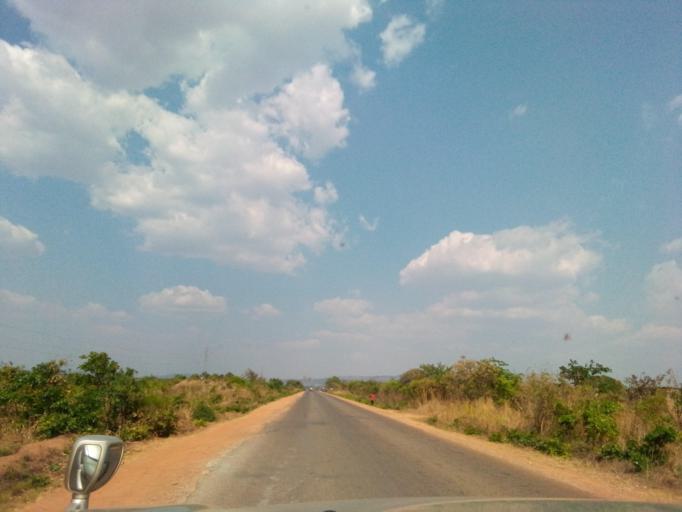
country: ZM
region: Northern
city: Mpika
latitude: -11.8331
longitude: 31.4063
